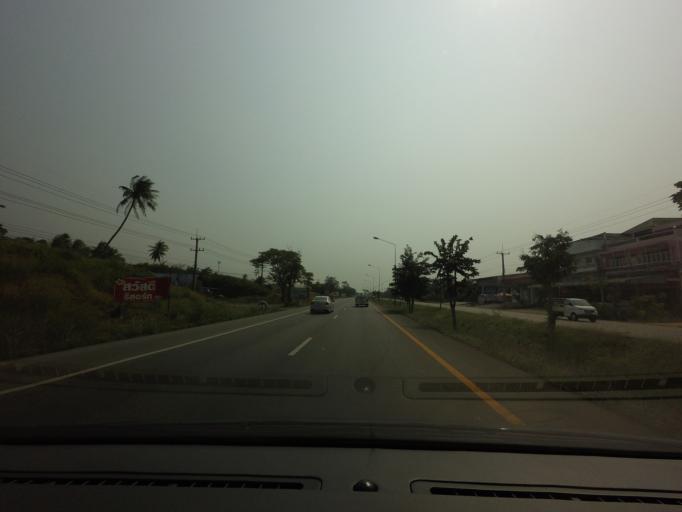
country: TH
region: Prachuap Khiri Khan
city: Sam Roi Yot
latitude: 12.2393
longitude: 99.8704
